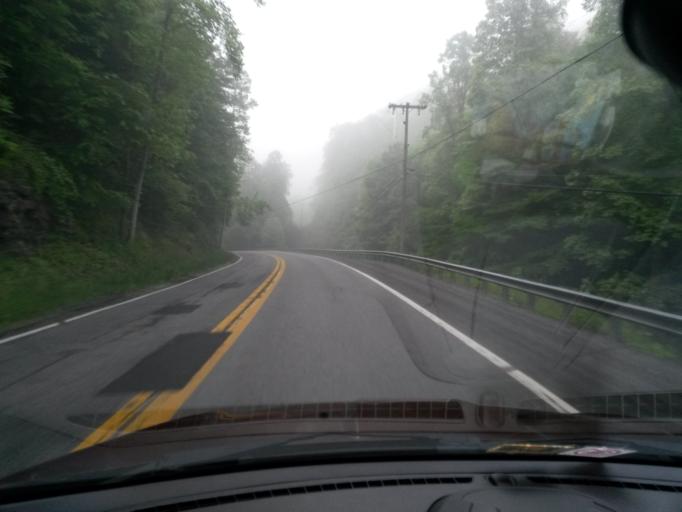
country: US
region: West Virginia
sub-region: McDowell County
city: Welch
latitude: 37.4551
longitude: -81.5433
